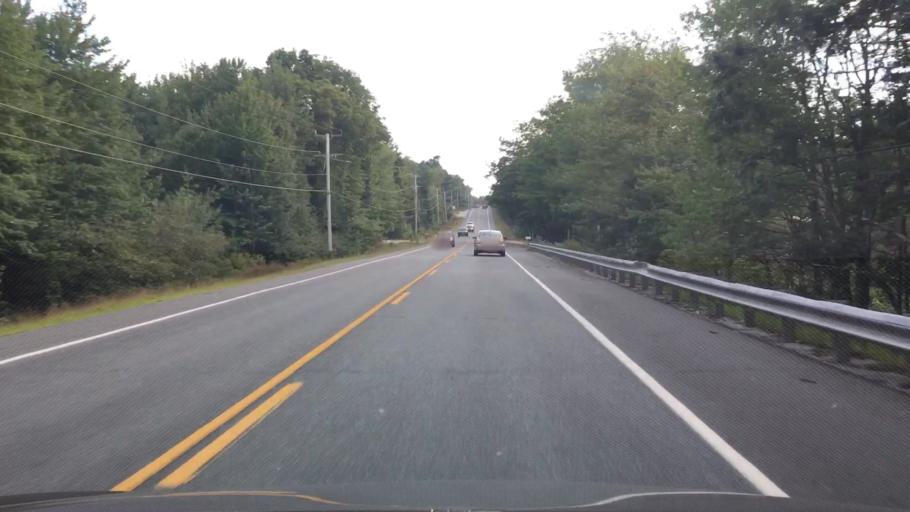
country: US
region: Maine
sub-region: Hancock County
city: Surry
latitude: 44.4501
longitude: -68.5578
